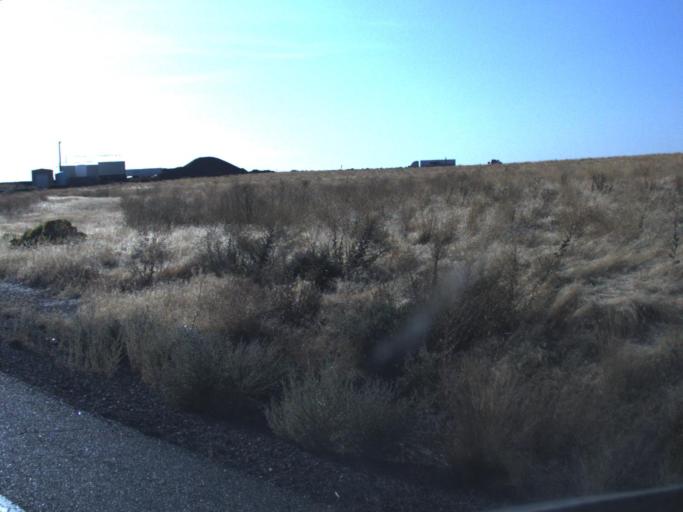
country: US
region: Washington
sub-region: Benton County
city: Highland
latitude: 46.1434
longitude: -119.1965
